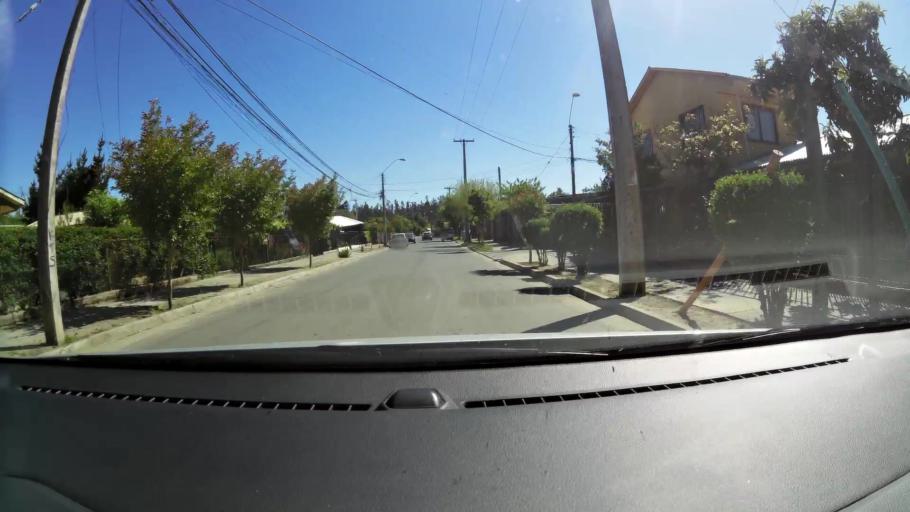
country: CL
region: Valparaiso
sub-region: Provincia de Marga Marga
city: Quilpue
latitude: -33.3157
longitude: -71.4050
